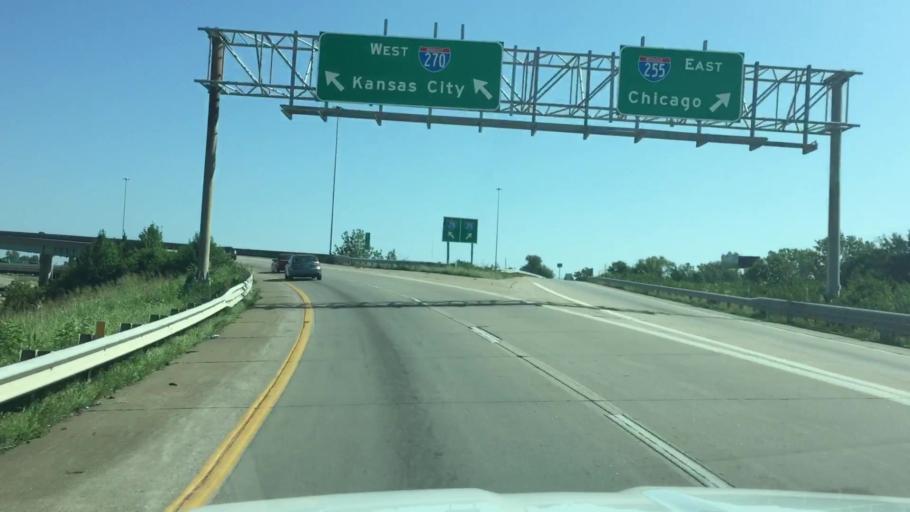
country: US
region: Missouri
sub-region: Saint Louis County
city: Mehlville
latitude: 38.5007
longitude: -90.3398
